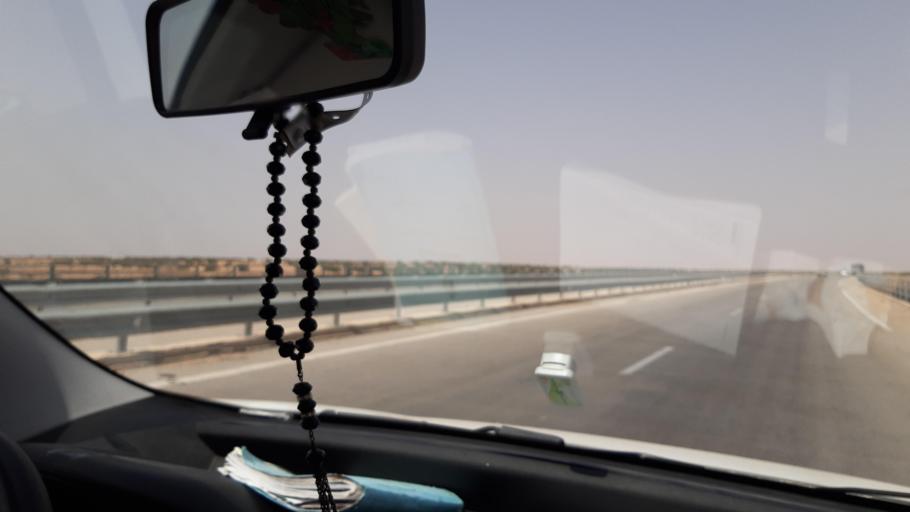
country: TN
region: Safaqis
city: Bi'r `Ali Bin Khalifah
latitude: 34.5189
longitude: 10.0783
